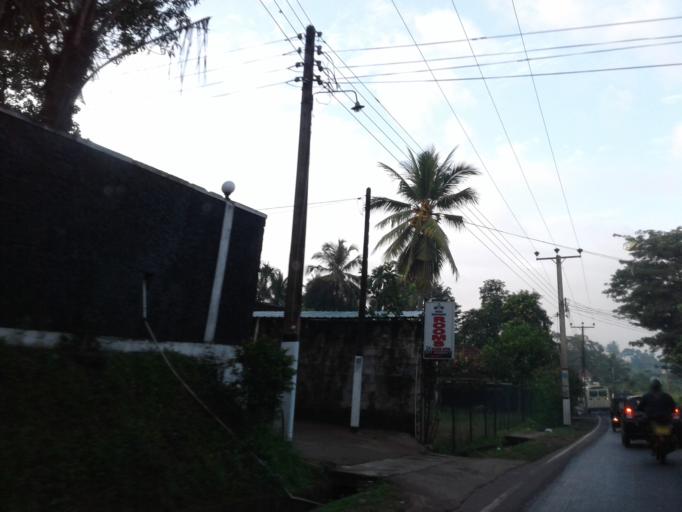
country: LK
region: Western
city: Mulleriyawa
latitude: 6.9646
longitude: 79.9974
